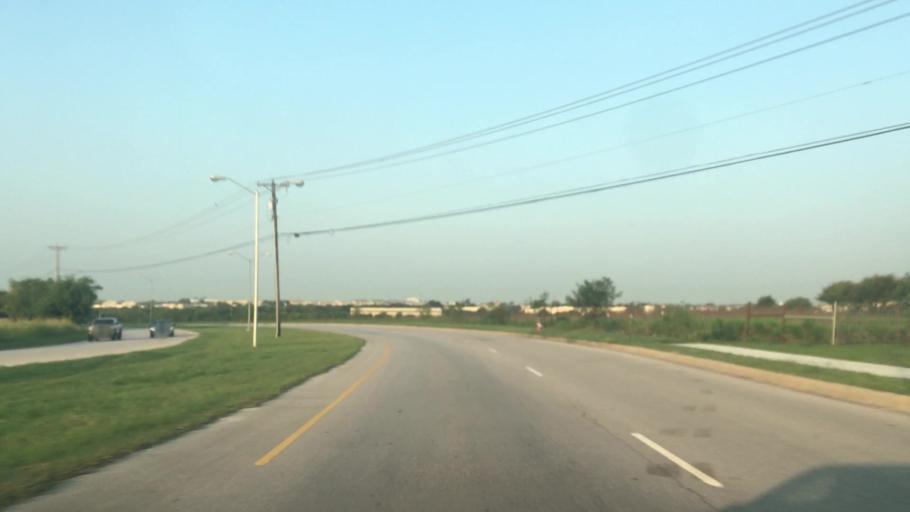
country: US
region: Texas
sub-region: Travis County
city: Windemere
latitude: 30.4796
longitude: -97.6622
